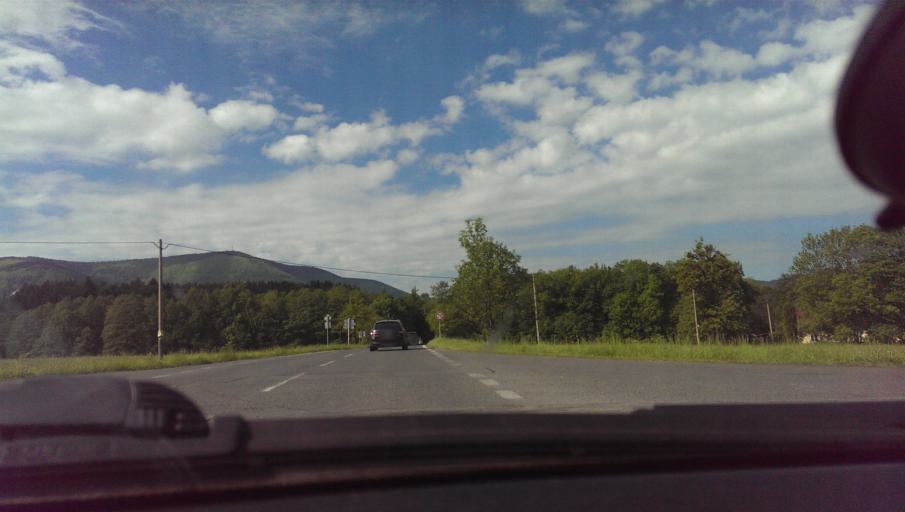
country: CZ
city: Trojanovice
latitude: 49.5286
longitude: 18.2486
